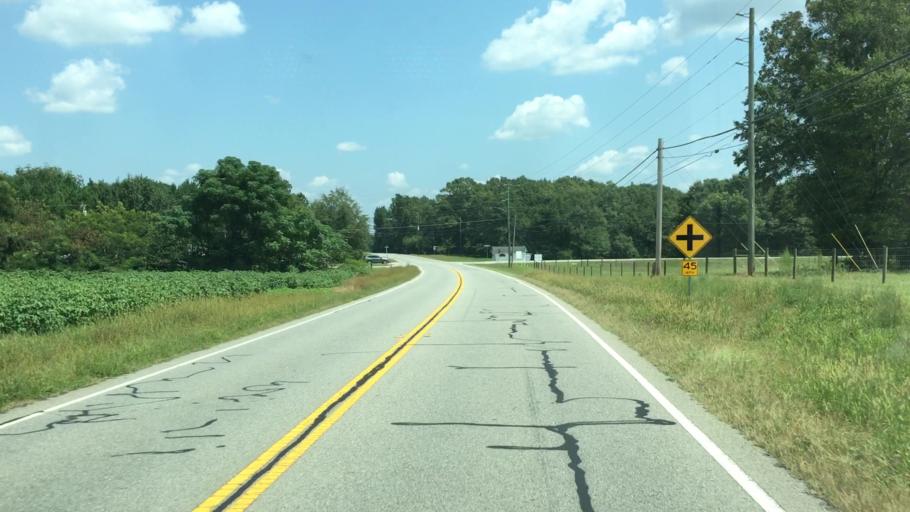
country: US
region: Georgia
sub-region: Oconee County
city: Bogart
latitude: 33.8710
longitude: -83.5070
